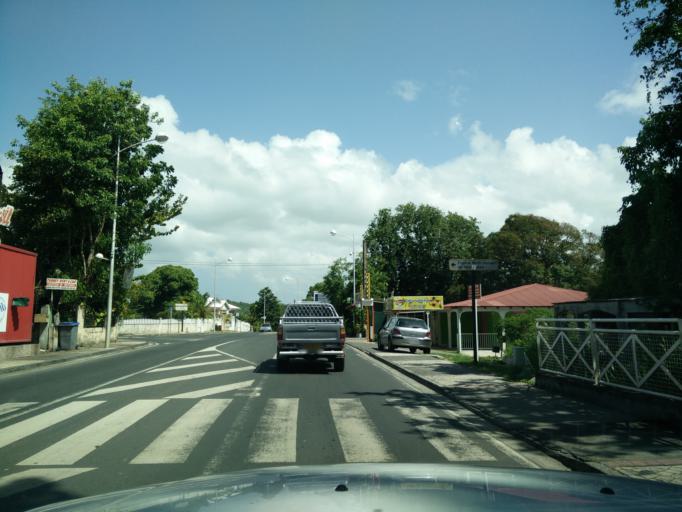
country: GP
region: Guadeloupe
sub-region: Guadeloupe
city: Le Gosier
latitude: 16.2078
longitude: -61.4998
